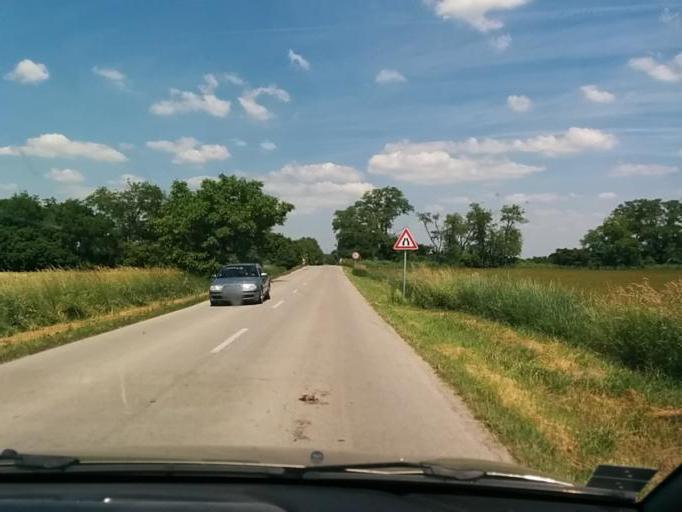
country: SK
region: Trnavsky
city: Sladkovicovo
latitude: 48.2149
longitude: 17.5503
